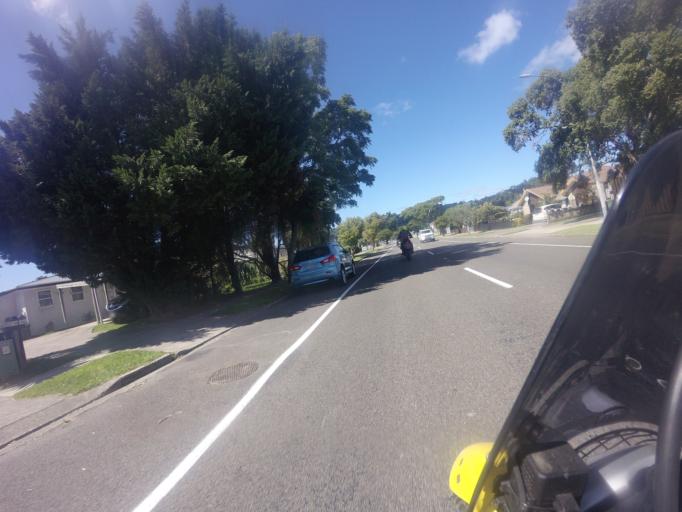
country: NZ
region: Bay of Plenty
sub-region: Whakatane District
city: Whakatane
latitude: -37.9535
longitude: 176.9847
